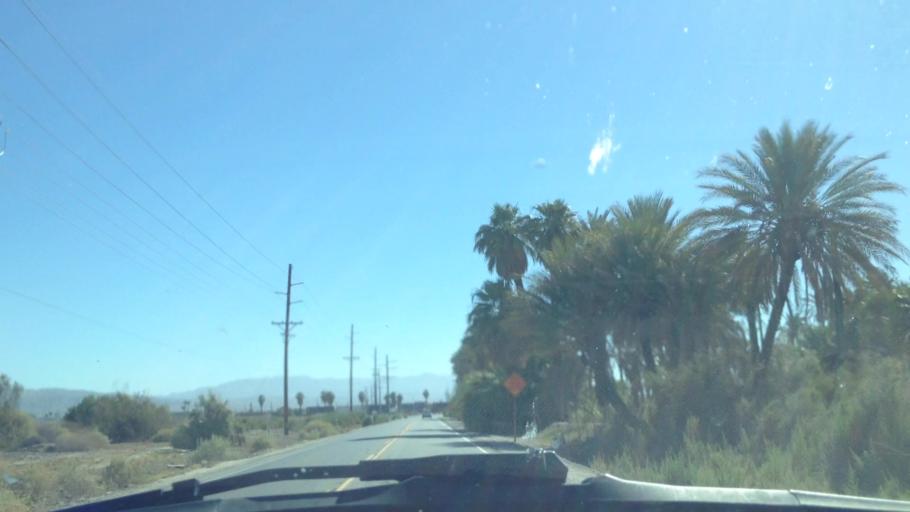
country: US
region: California
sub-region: Riverside County
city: Mecca
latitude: 33.5693
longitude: -116.0833
